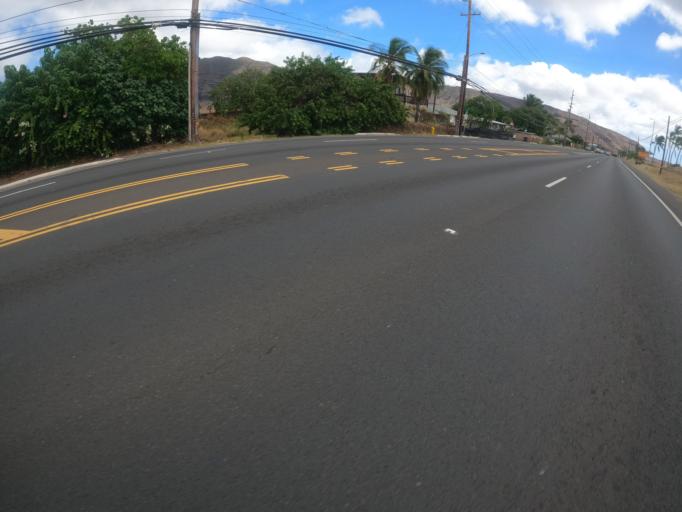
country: US
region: Hawaii
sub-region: Honolulu County
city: Nanakuli
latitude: 21.3911
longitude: -158.1558
